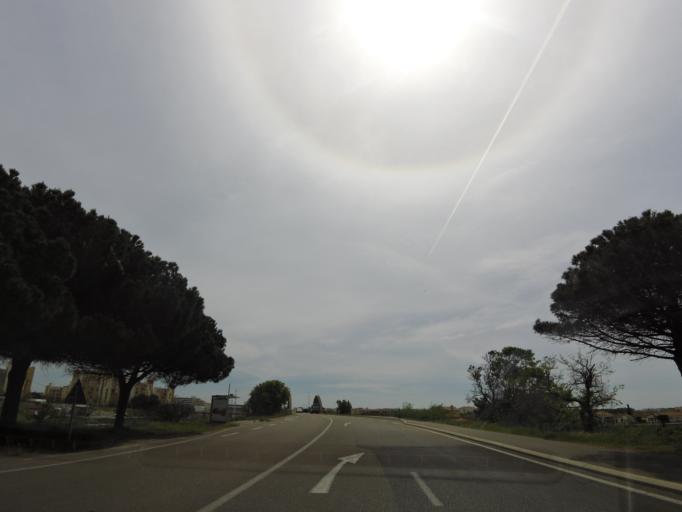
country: FR
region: Languedoc-Roussillon
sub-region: Departement de l'Herault
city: Perols
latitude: 43.5485
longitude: 3.9693
